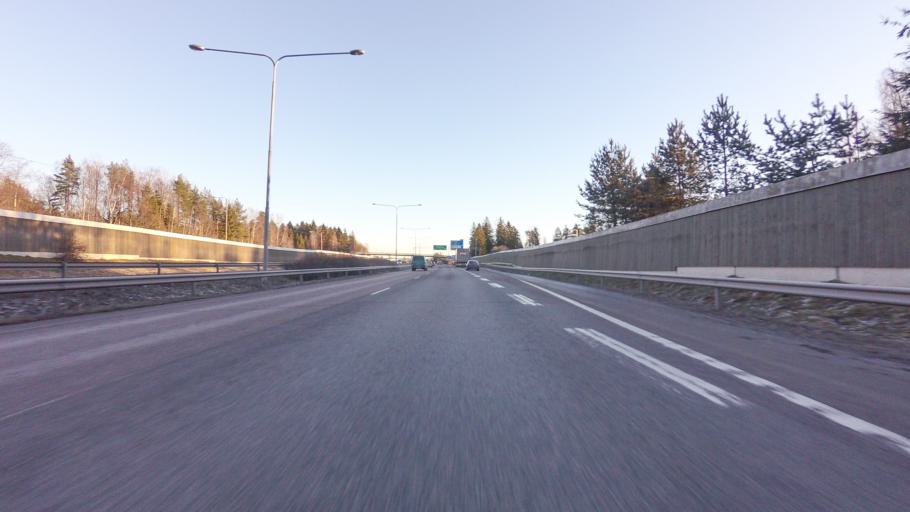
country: FI
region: Uusimaa
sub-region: Helsinki
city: Espoo
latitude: 60.2217
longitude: 24.6321
